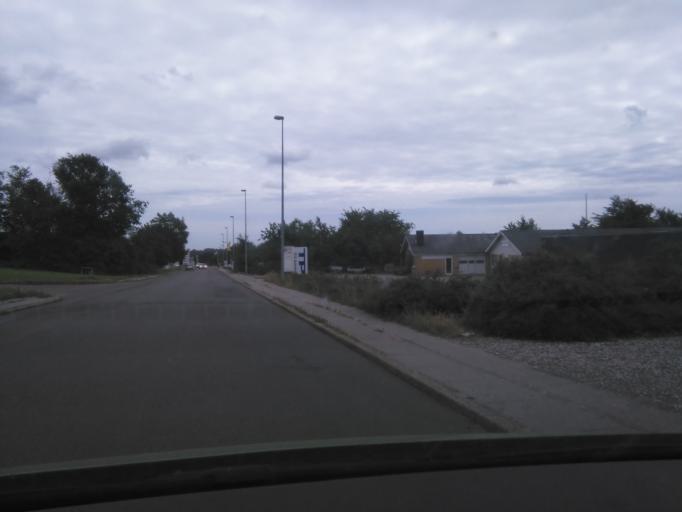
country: DK
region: Central Jutland
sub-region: Odder Kommune
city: Odder
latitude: 55.9860
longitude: 10.1402
